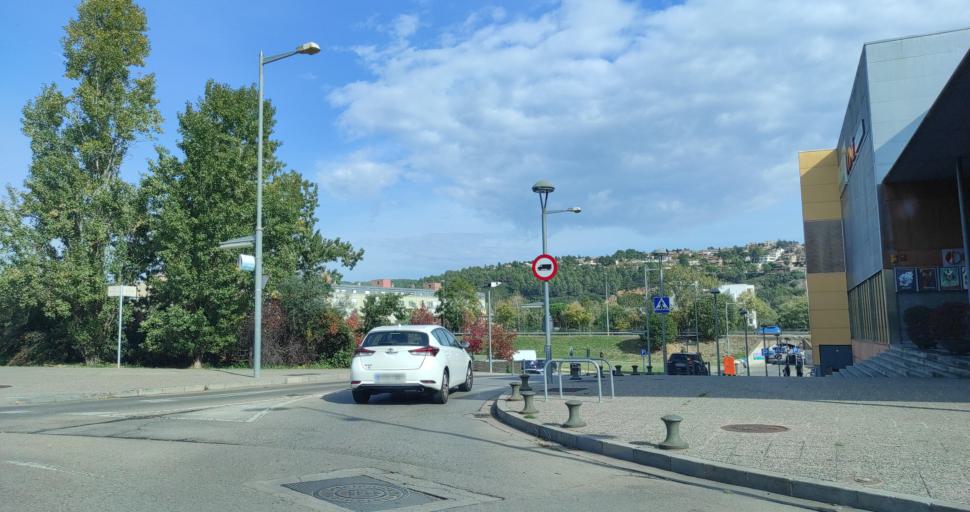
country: ES
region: Catalonia
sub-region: Provincia de Girona
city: Girona
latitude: 41.9921
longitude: 2.8182
